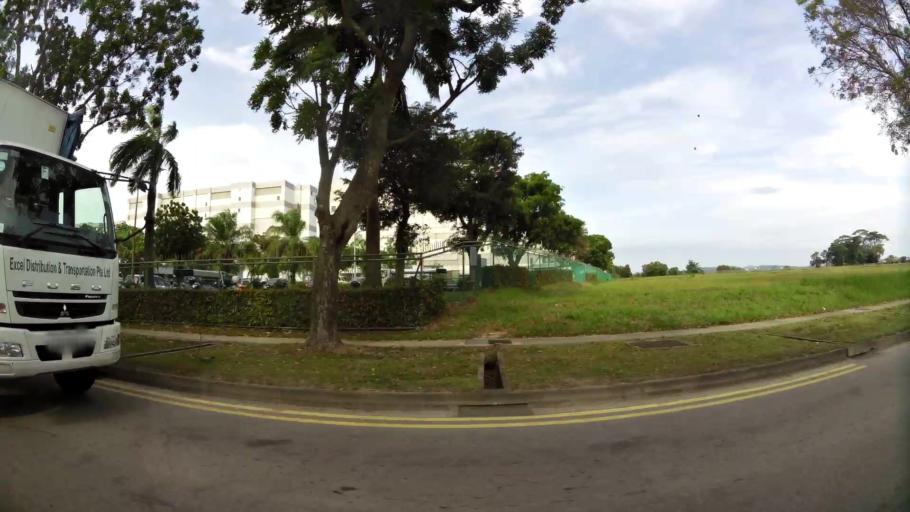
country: MY
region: Johor
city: Johor Bahru
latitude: 1.3336
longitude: 103.6344
